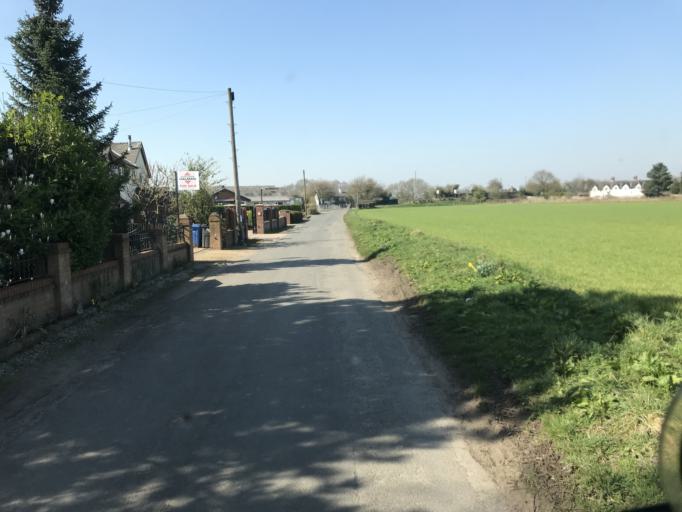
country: GB
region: England
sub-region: Warrington
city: Lymm
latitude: 53.4237
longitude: -2.4730
